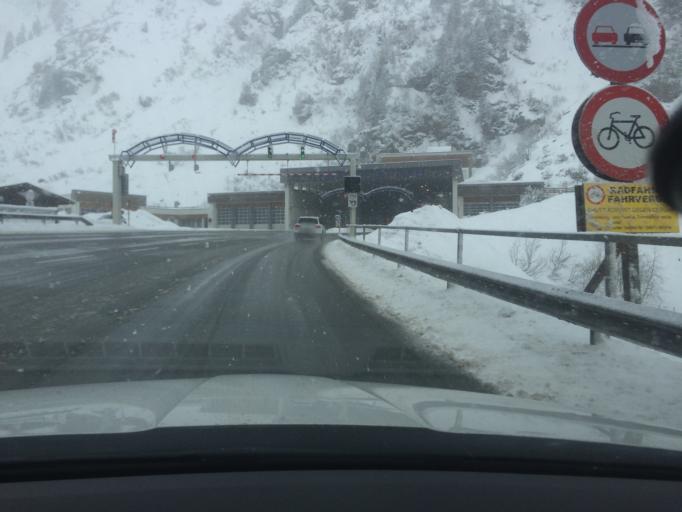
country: AT
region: Salzburg
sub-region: Politischer Bezirk Zell am See
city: Stuhlfelden
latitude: 47.1612
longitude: 12.5369
